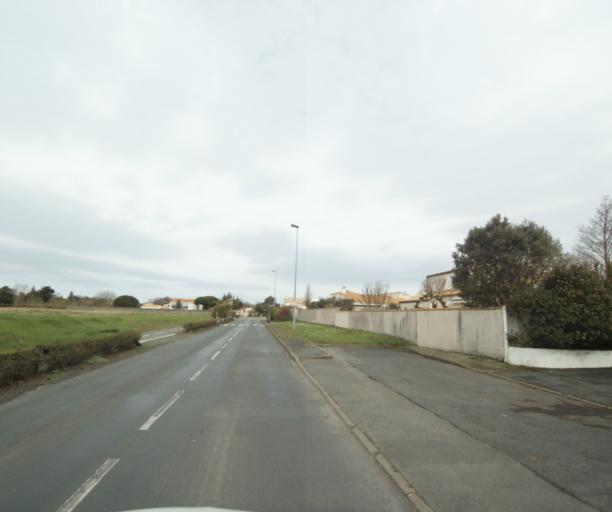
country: FR
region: Poitou-Charentes
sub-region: Departement de la Charente-Maritime
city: Lagord
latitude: 46.1834
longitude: -1.1666
